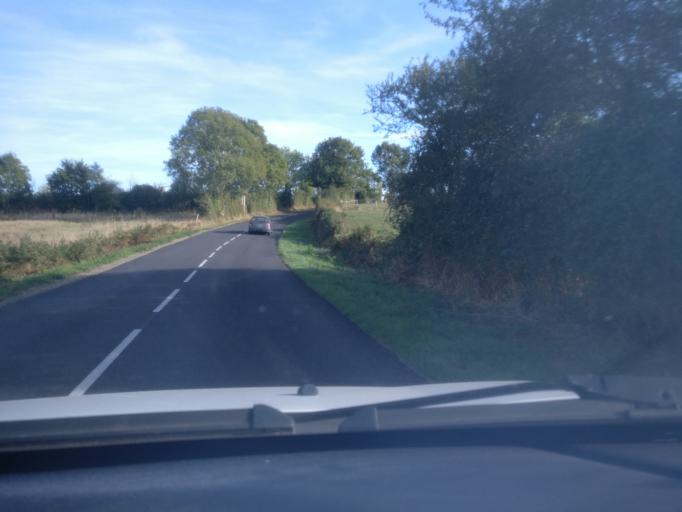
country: FR
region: Lower Normandy
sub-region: Departement de la Manche
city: Sartilly
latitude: 48.7172
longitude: -1.5020
